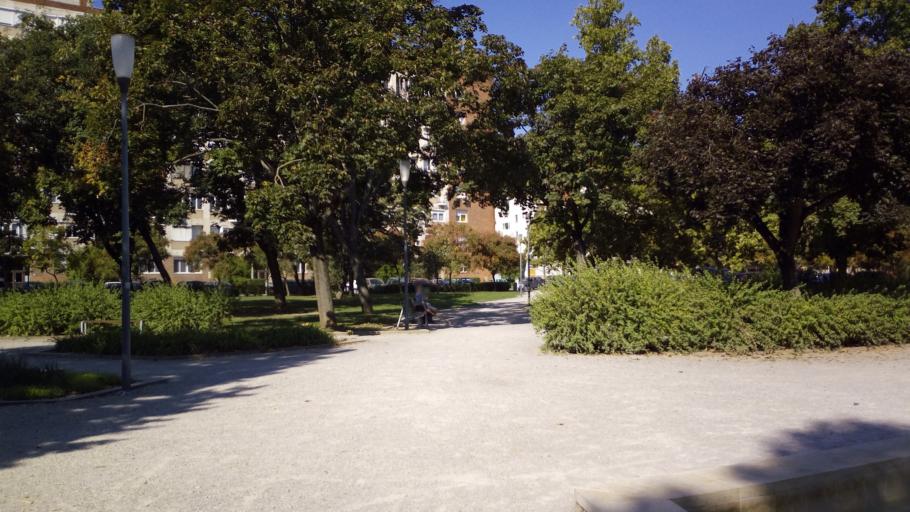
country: HU
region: Baranya
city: Pecs
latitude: 46.0633
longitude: 18.1989
